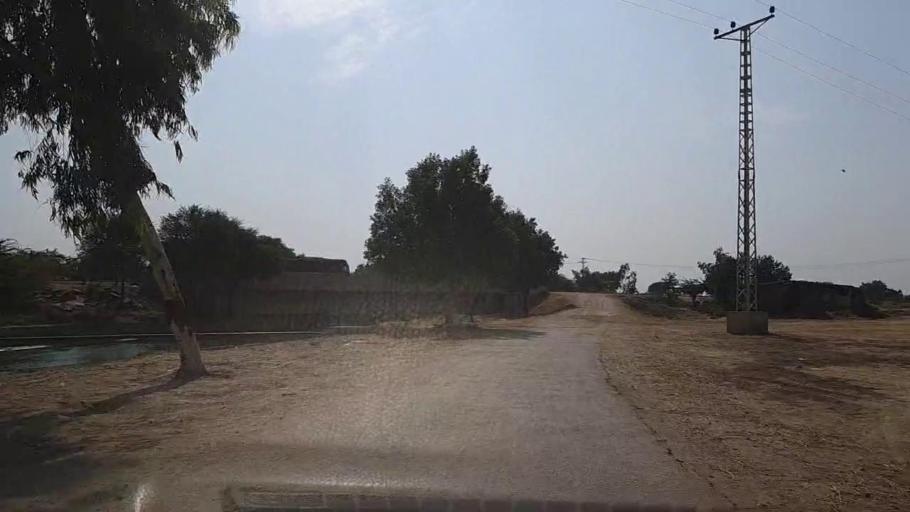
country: PK
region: Sindh
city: Thatta
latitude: 24.7407
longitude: 67.7641
